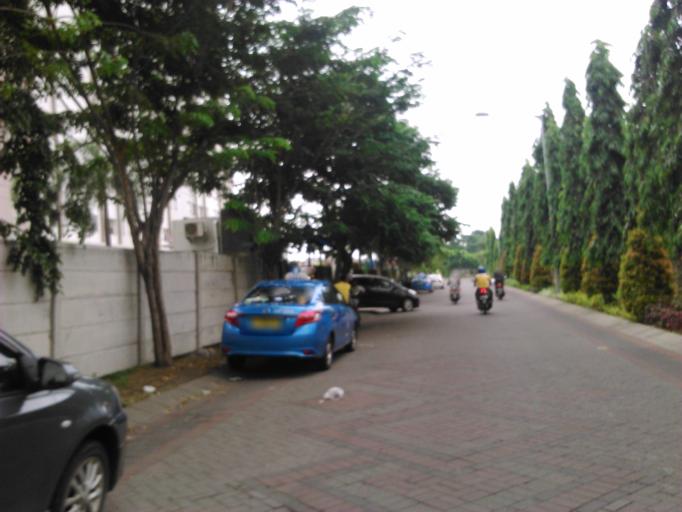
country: ID
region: East Java
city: Semampir
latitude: -7.2886
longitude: 112.7875
